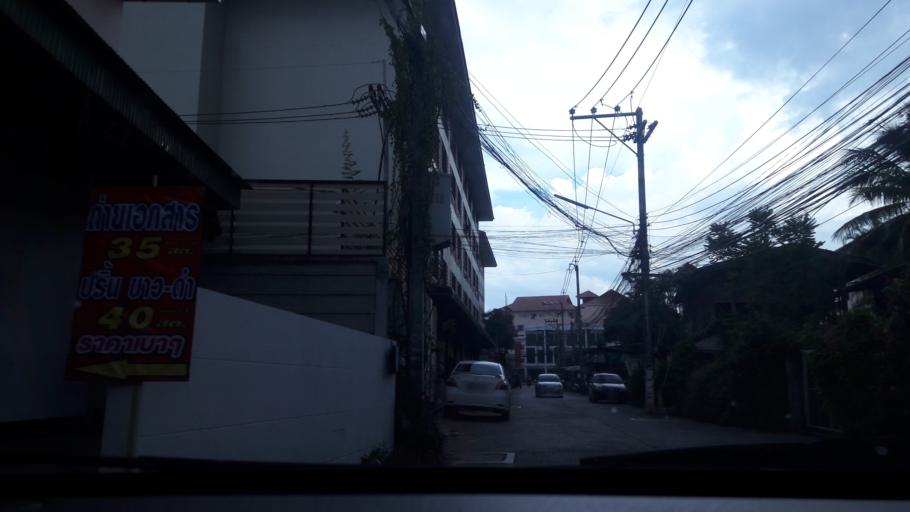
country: TH
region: Chiang Mai
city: Chiang Mai
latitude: 18.8074
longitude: 98.9809
